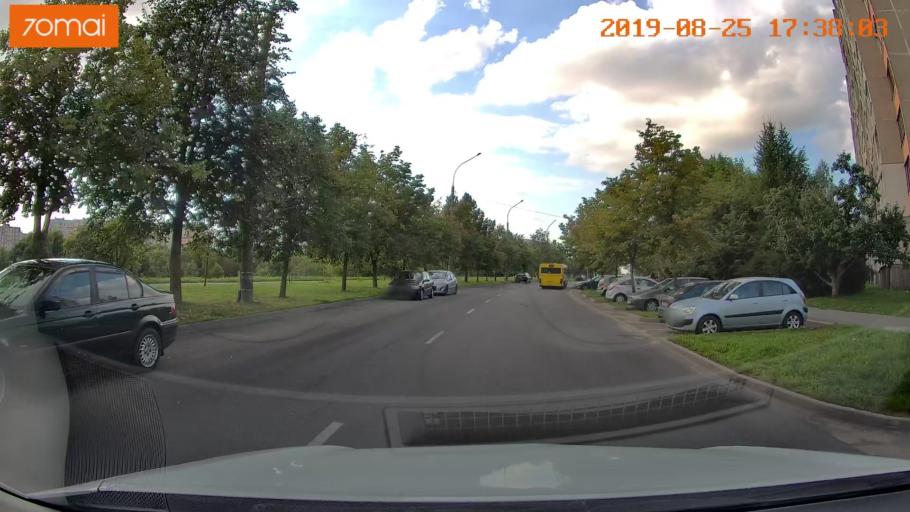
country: BY
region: Minsk
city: Malinovka
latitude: 53.8606
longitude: 27.4495
